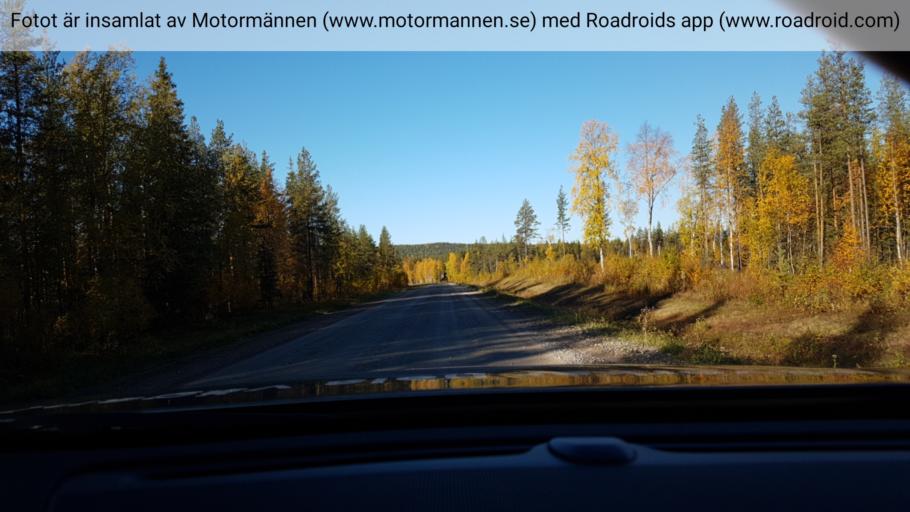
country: SE
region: Norrbotten
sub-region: Alvsbyns Kommun
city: AElvsbyn
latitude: 66.2780
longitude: 21.1118
